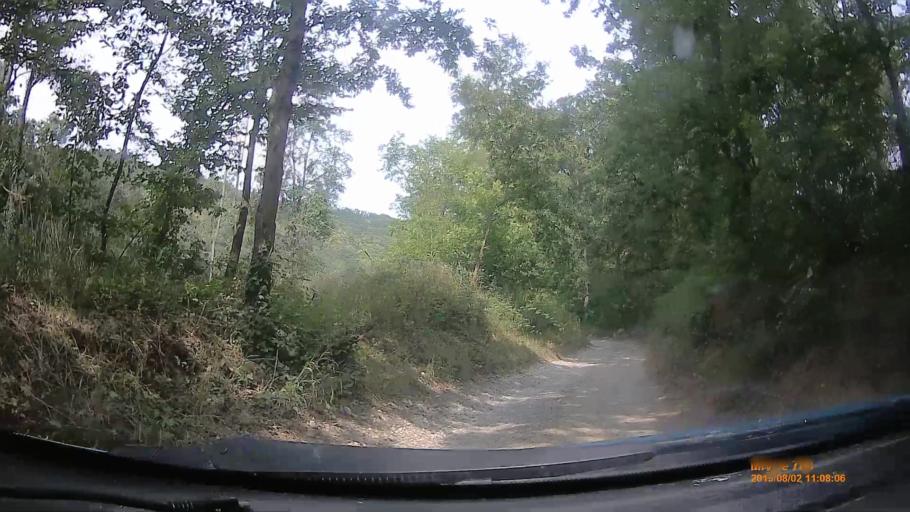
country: HU
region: Baranya
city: Buekkoesd
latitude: 46.0999
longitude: 17.9445
